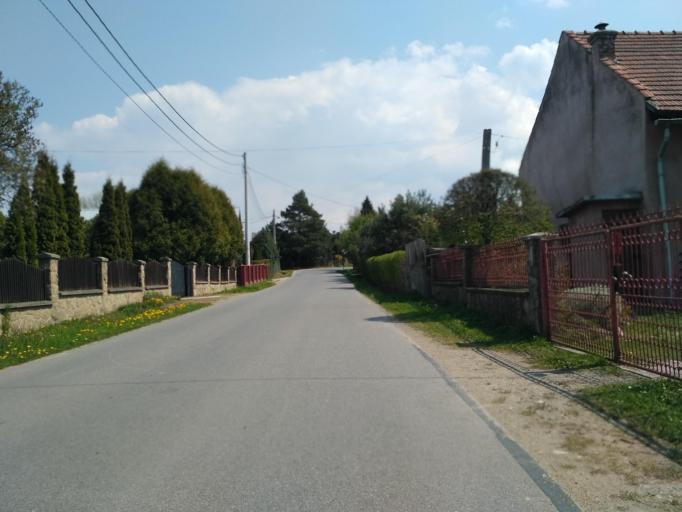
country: PL
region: Subcarpathian Voivodeship
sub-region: Powiat jasielski
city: Tarnowiec
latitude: 49.7435
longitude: 21.5861
